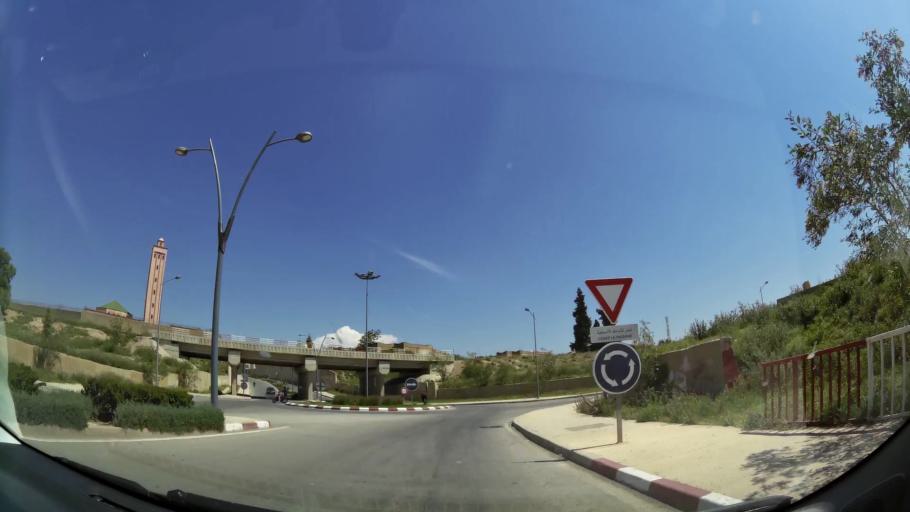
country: MA
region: Oriental
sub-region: Oujda-Angad
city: Oujda
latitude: 34.6929
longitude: -1.9243
